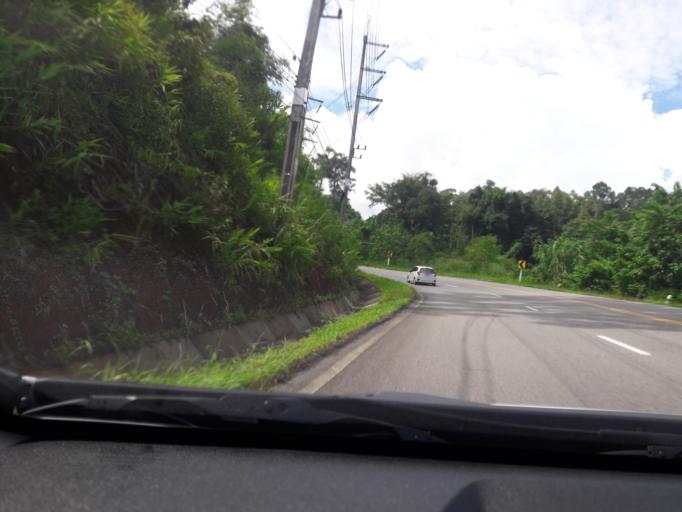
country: TH
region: Chiang Mai
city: Mae Taeng
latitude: 19.1249
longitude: 98.7683
